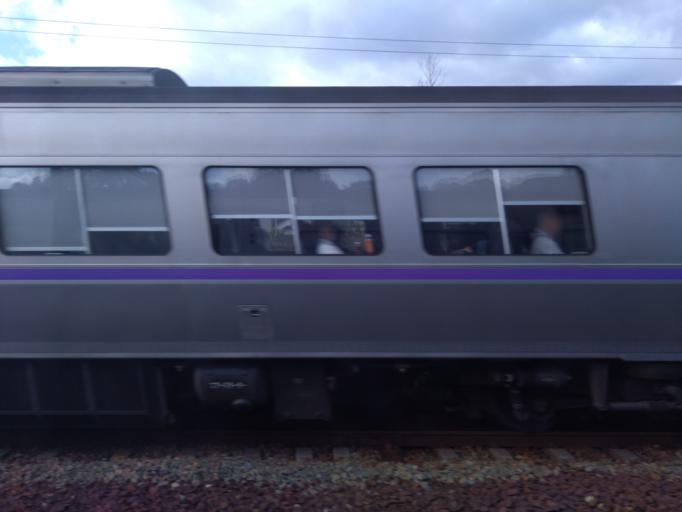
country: JP
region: Hokkaido
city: Shiraoi
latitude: 42.4514
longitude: 141.1796
